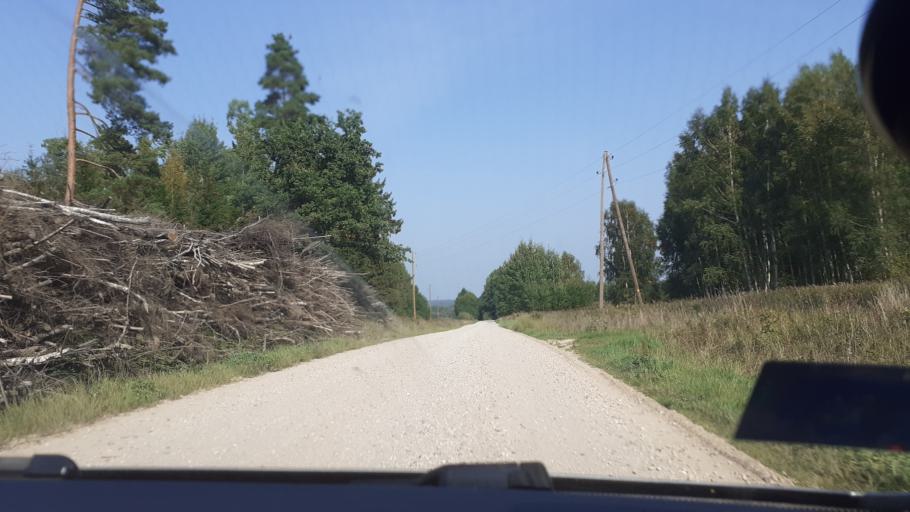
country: LV
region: Kuldigas Rajons
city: Kuldiga
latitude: 56.9813
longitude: 21.8585
